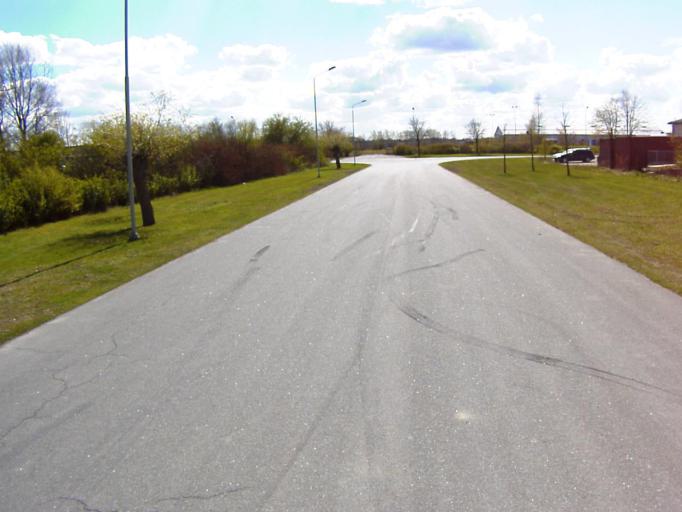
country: SE
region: Skane
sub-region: Kristianstads Kommun
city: Kristianstad
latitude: 56.0133
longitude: 14.1218
